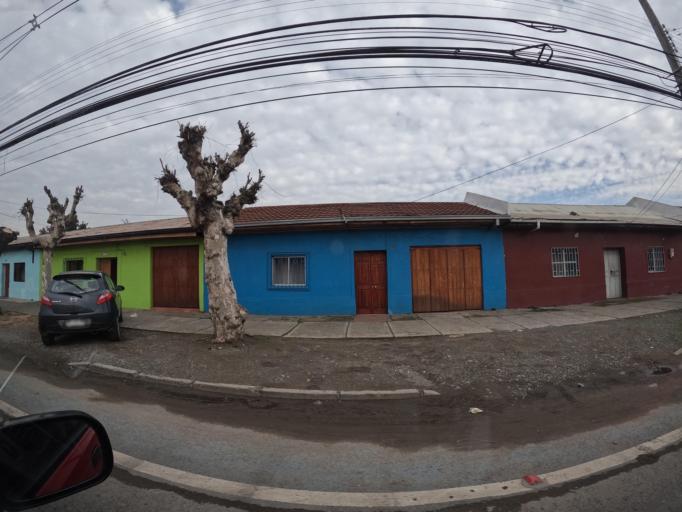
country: CL
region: Maule
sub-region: Provincia de Linares
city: Linares
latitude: -35.8424
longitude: -71.5841
